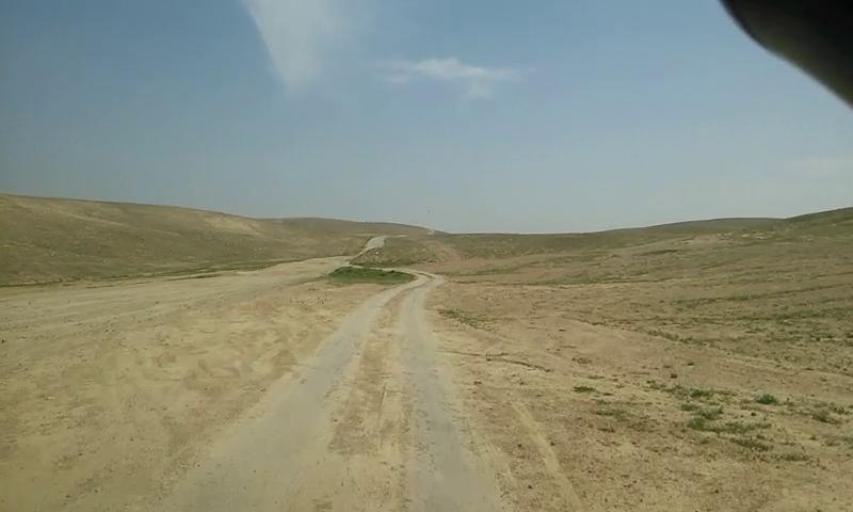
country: PS
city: `Arab ar Rashaydah
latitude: 31.5289
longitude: 35.2904
